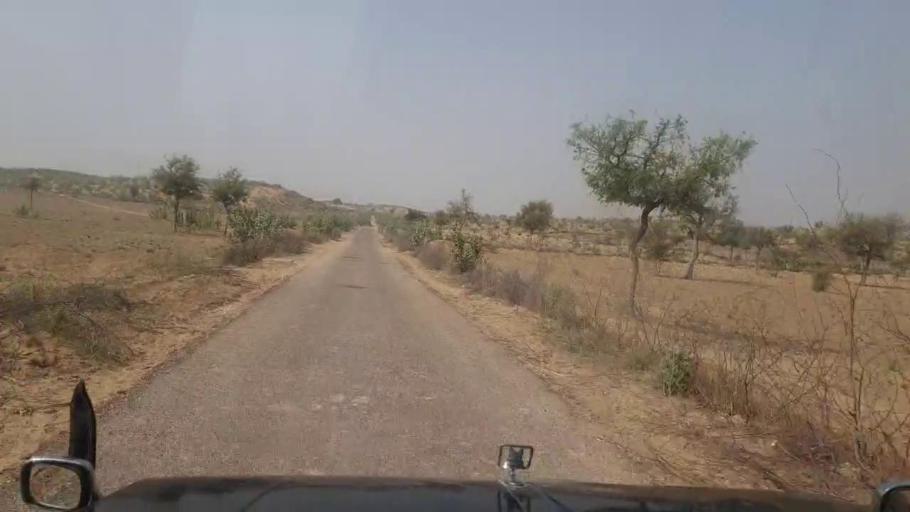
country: PK
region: Sindh
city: Islamkot
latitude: 25.0884
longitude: 70.1582
